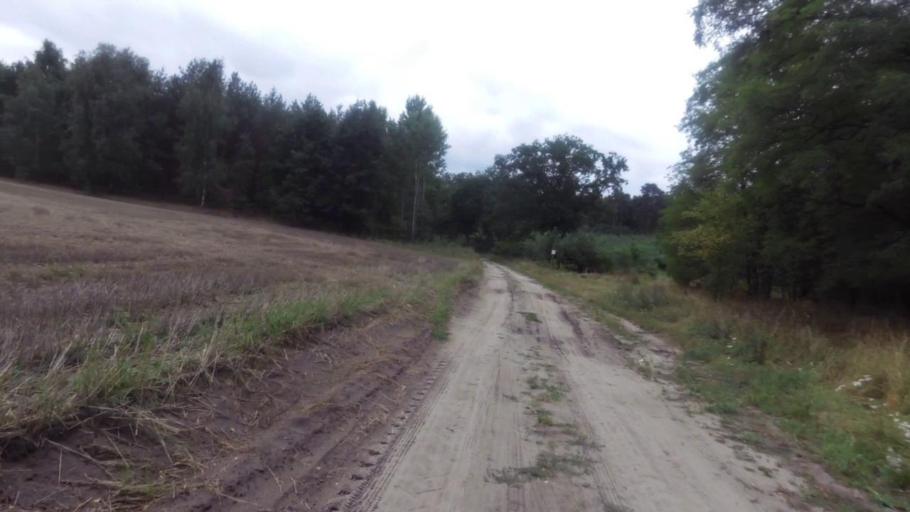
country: PL
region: West Pomeranian Voivodeship
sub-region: Powiat mysliborski
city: Boleszkowice
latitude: 52.6715
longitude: 14.6164
